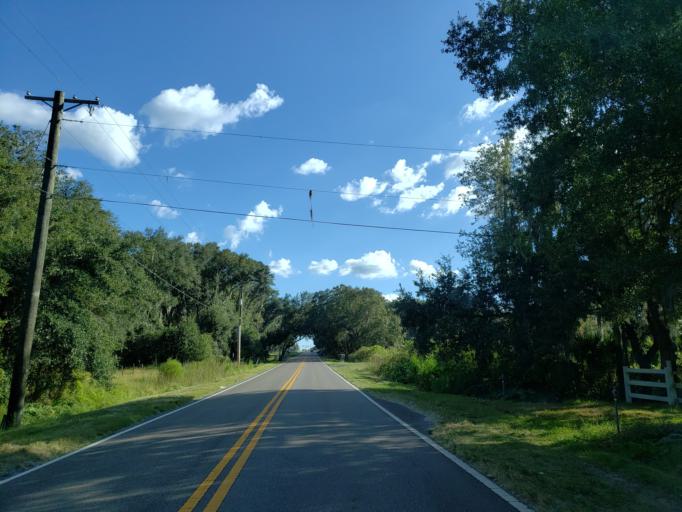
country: US
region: Florida
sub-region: Hillsborough County
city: Valrico
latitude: 27.9440
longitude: -82.2196
